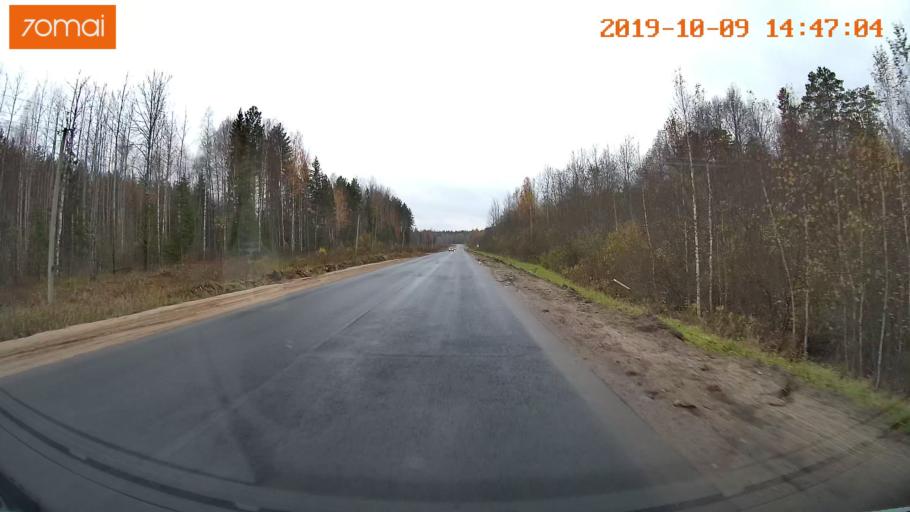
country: RU
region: Kostroma
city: Buy
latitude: 58.4227
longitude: 41.5742
